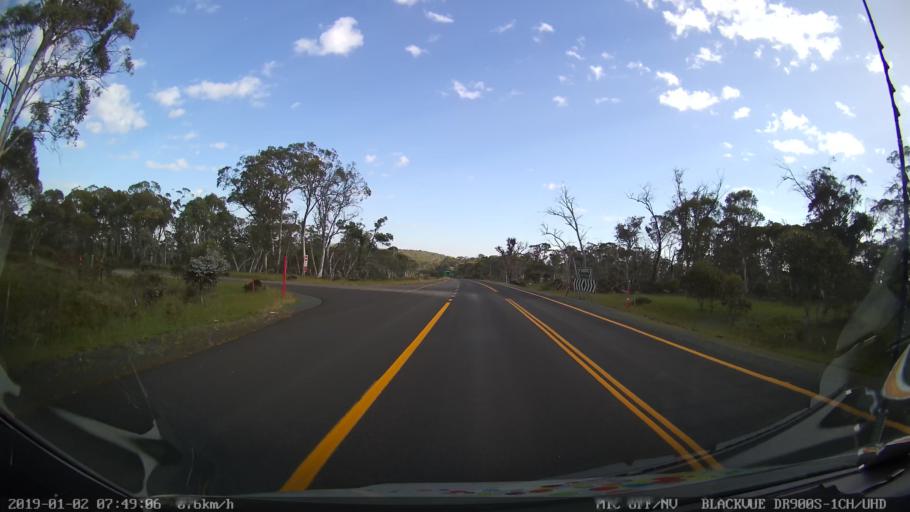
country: AU
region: New South Wales
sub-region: Tumut Shire
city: Tumut
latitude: -35.7456
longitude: 148.5213
